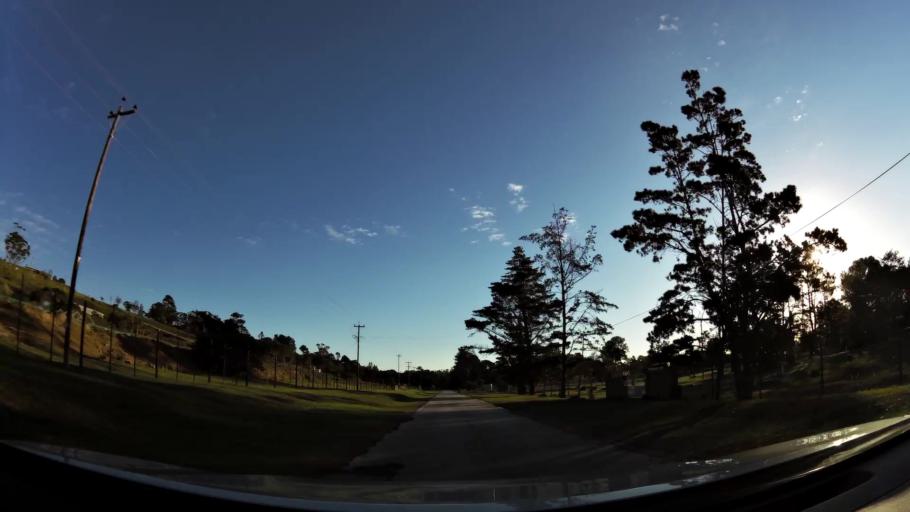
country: ZA
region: Eastern Cape
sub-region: Nelson Mandela Bay Metropolitan Municipality
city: Port Elizabeth
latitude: -33.9870
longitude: 25.4897
